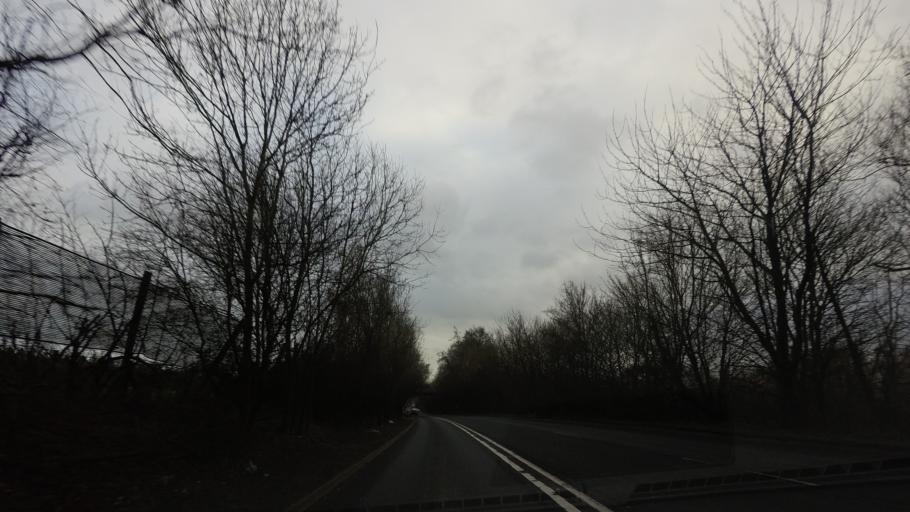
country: GB
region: England
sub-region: Kent
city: East Peckham
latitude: 51.2417
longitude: 0.3769
